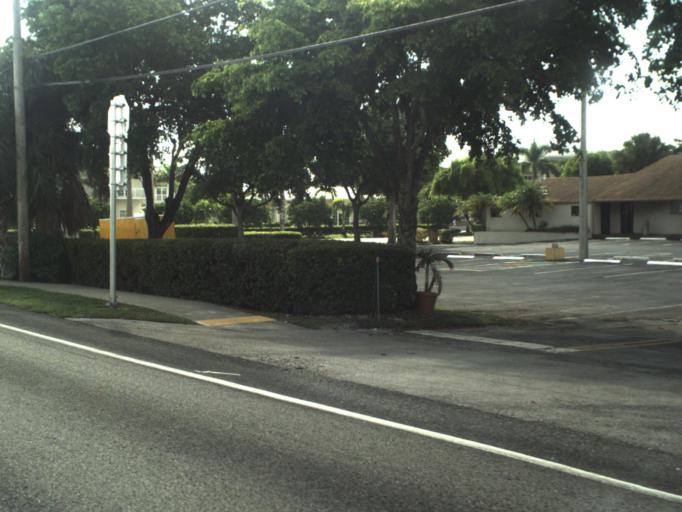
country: US
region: Florida
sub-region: Broward County
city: Melrose Park
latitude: 26.0862
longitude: -80.1771
